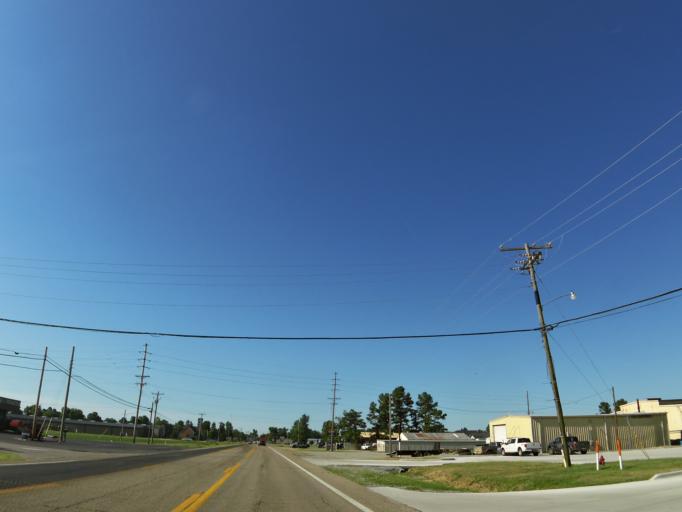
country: US
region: Arkansas
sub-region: Clay County
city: Corning
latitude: 36.4224
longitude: -90.5862
